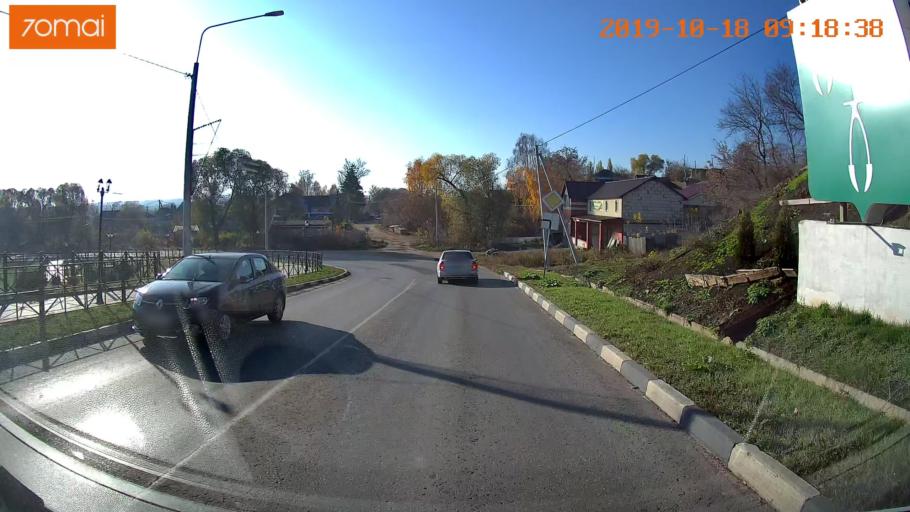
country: RU
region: Tula
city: Yefremov
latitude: 53.1355
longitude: 38.1206
